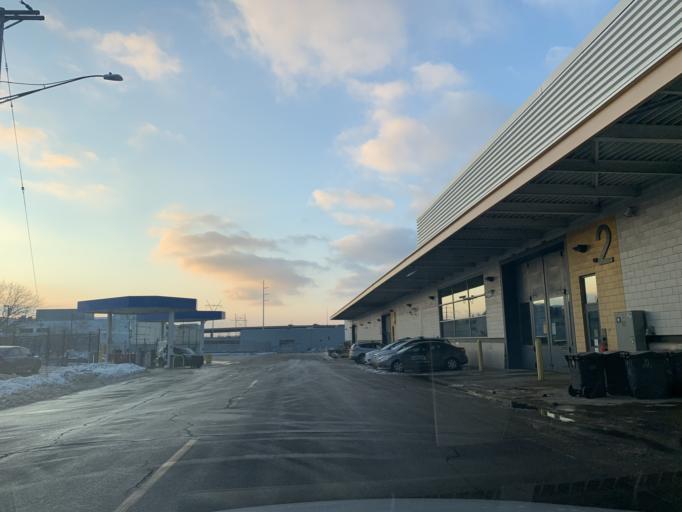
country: US
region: Minnesota
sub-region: Hennepin County
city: Minneapolis
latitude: 44.9780
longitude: -93.2825
